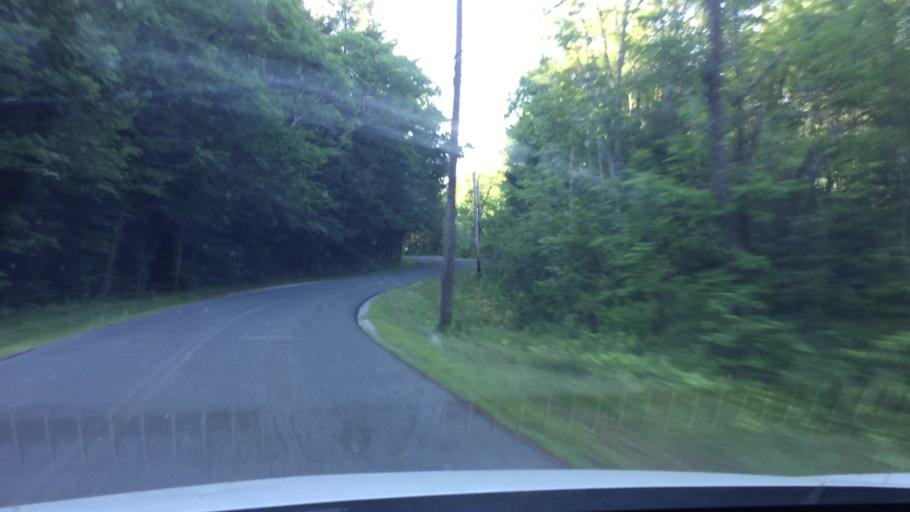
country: US
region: Massachusetts
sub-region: Berkshire County
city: Lee
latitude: 42.2784
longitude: -73.2087
